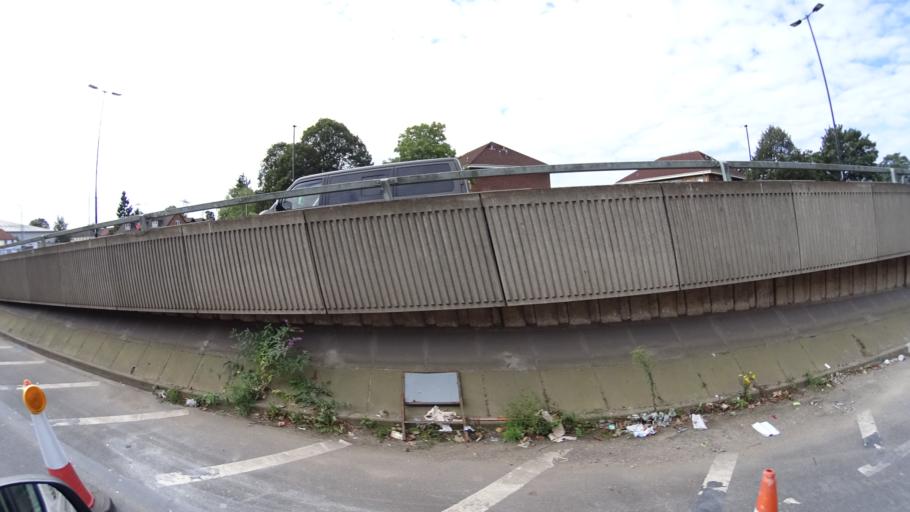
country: GB
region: England
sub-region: Hampshire
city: Totton
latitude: 50.9220
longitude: -1.4684
